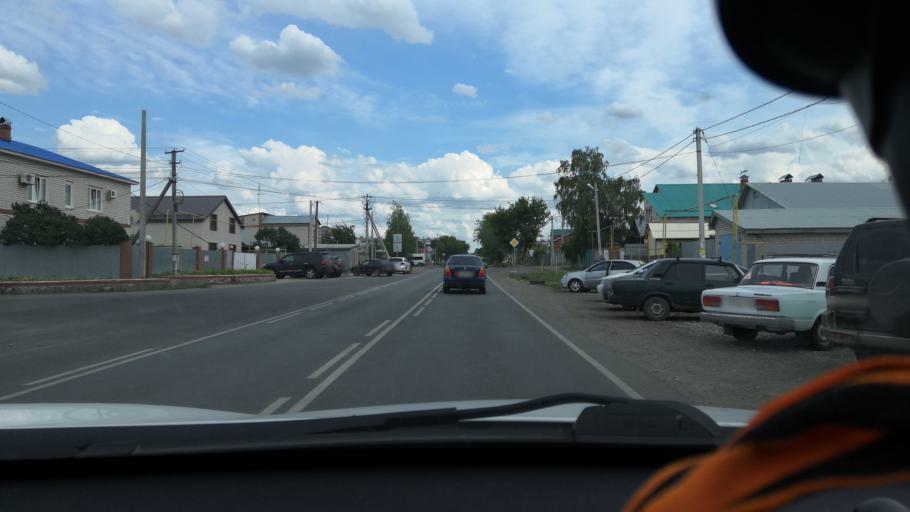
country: RU
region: Samara
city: Novosemeykino
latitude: 53.3754
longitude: 50.3472
